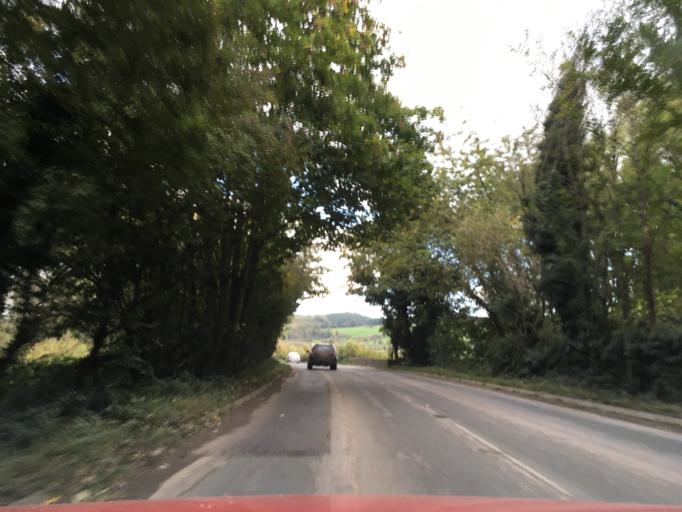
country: GB
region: England
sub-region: Herefordshire
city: Withington
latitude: 52.0604
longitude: -2.6229
